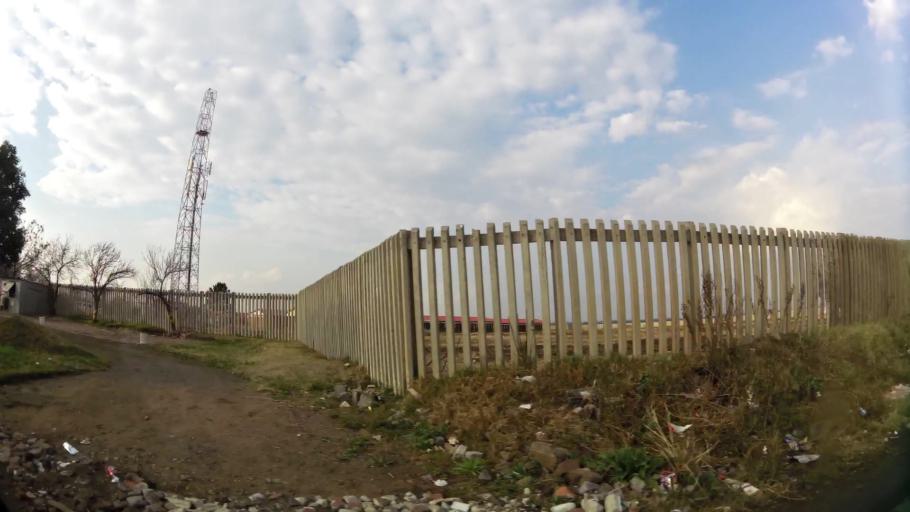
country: ZA
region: Gauteng
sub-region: Sedibeng District Municipality
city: Vanderbijlpark
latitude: -26.6924
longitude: 27.8773
